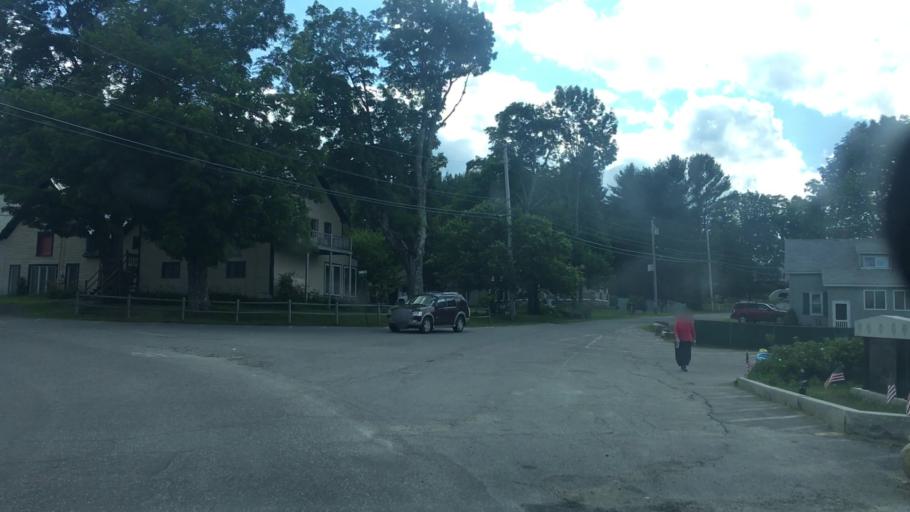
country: US
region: Maine
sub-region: Franklin County
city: Farmington
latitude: 44.7160
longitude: -70.0817
